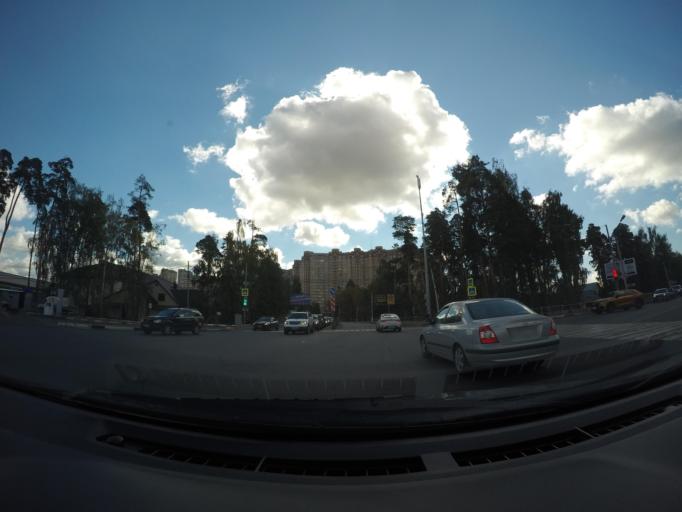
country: RU
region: Moskovskaya
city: Ramenskoye
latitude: 55.5828
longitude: 38.2095
